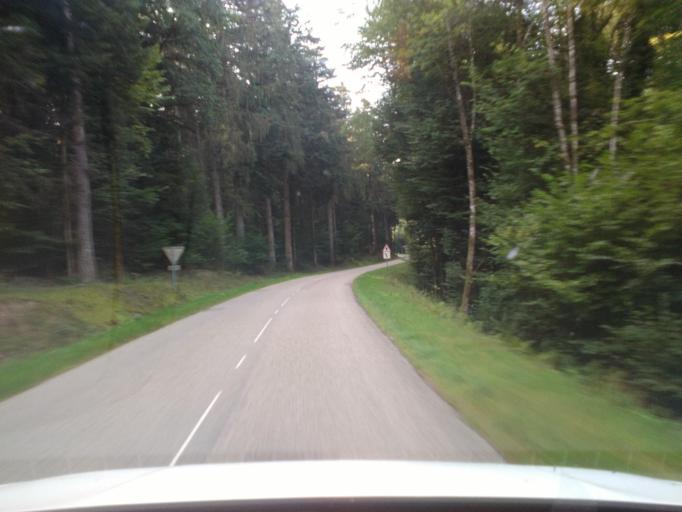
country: FR
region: Lorraine
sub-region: Departement des Vosges
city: Senones
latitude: 48.4024
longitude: 7.0202
